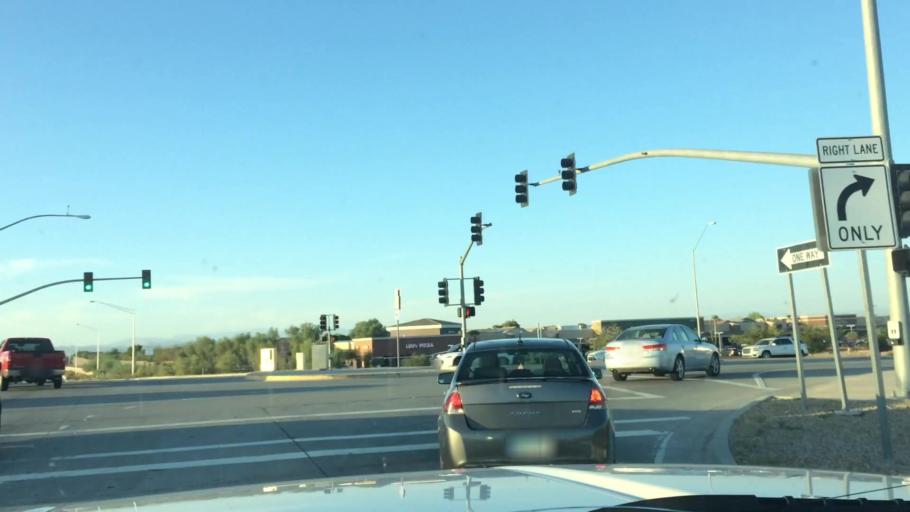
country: US
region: Arizona
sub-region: Maricopa County
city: Citrus Park
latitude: 33.6238
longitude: -112.4173
